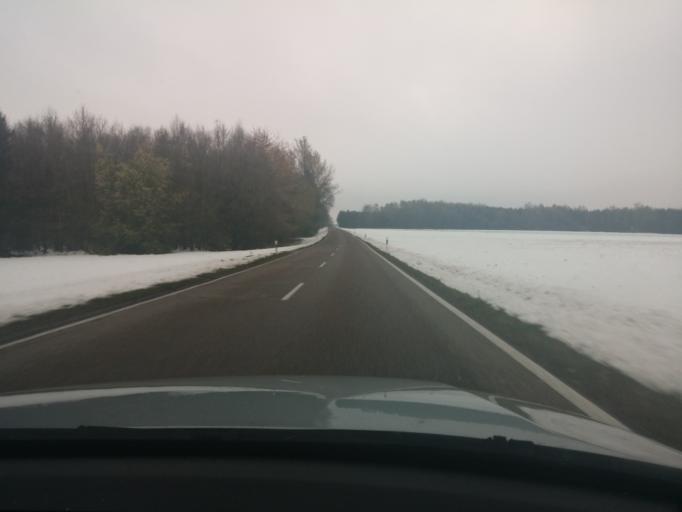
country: DE
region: Bavaria
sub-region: Swabia
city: Kronburg
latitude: 47.9188
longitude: 10.1517
